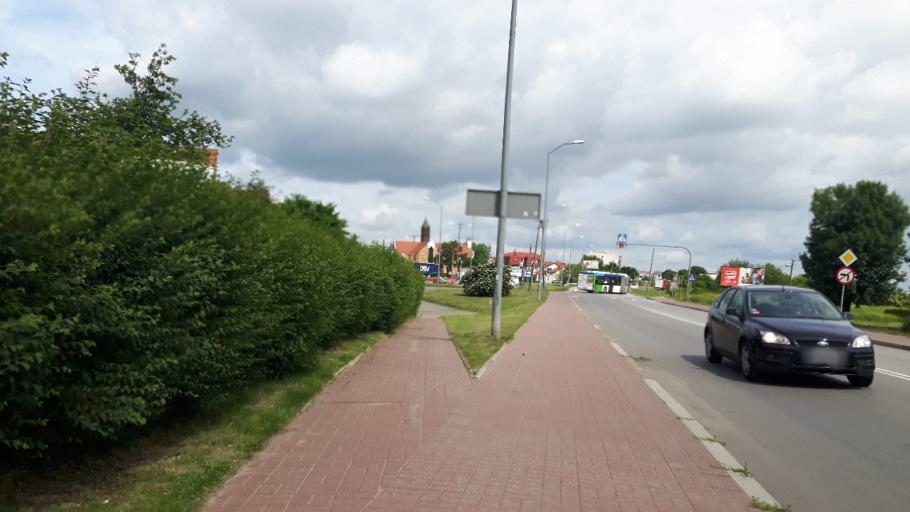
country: PL
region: West Pomeranian Voivodeship
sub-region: Powiat policki
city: Przeclaw
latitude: 53.3730
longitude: 14.4726
